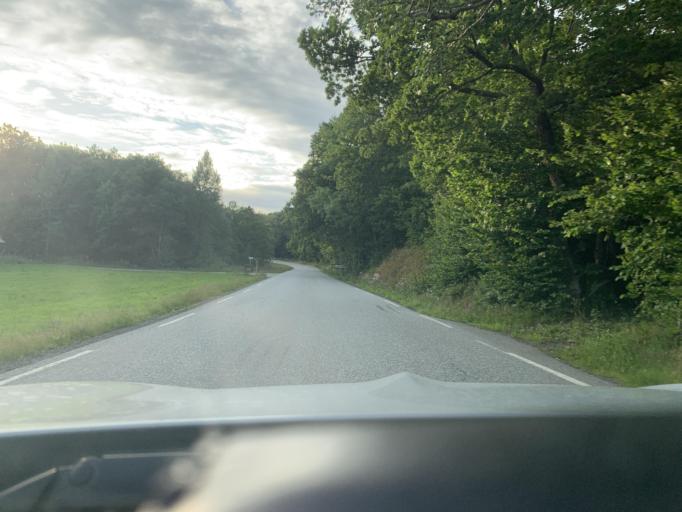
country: NO
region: Rogaland
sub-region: Time
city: Bryne
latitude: 58.6895
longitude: 5.7231
